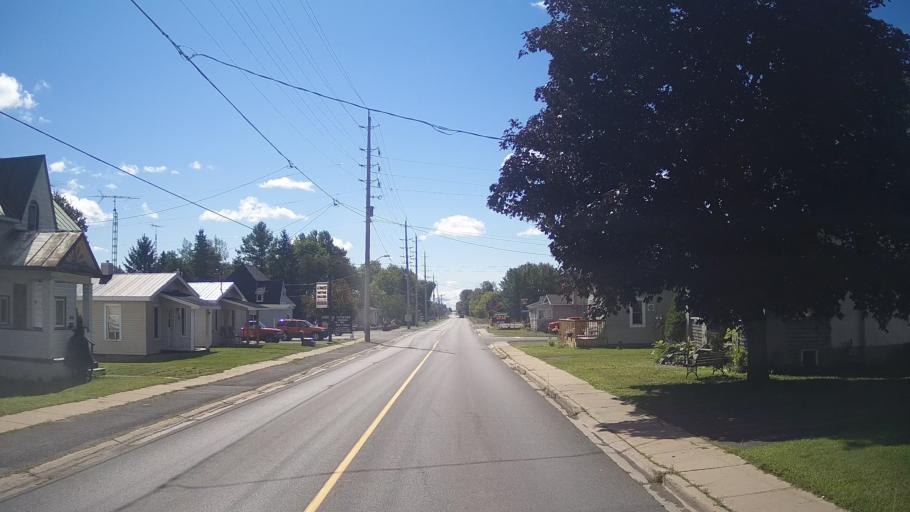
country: US
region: New York
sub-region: St. Lawrence County
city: Norfolk
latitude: 44.9736
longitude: -75.2427
